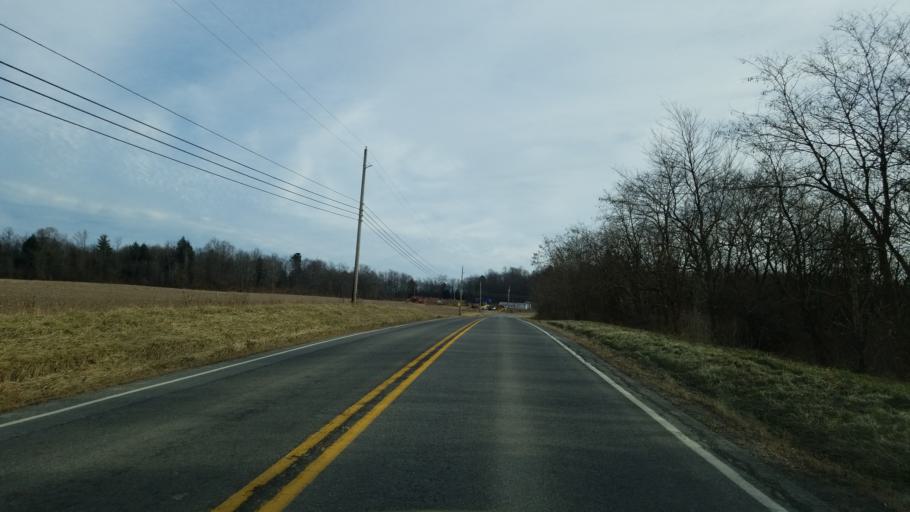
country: US
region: Pennsylvania
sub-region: Indiana County
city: Johnsonburg
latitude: 40.9201
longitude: -78.8532
